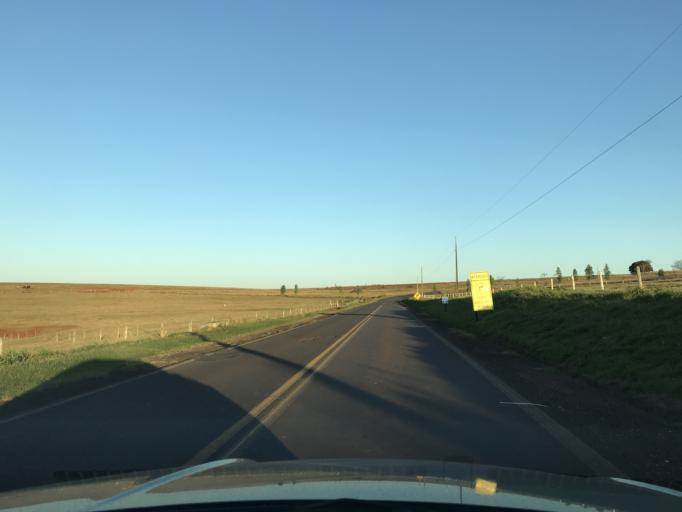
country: PY
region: Canindeyu
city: Salto del Guaira
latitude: -24.0843
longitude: -54.0926
